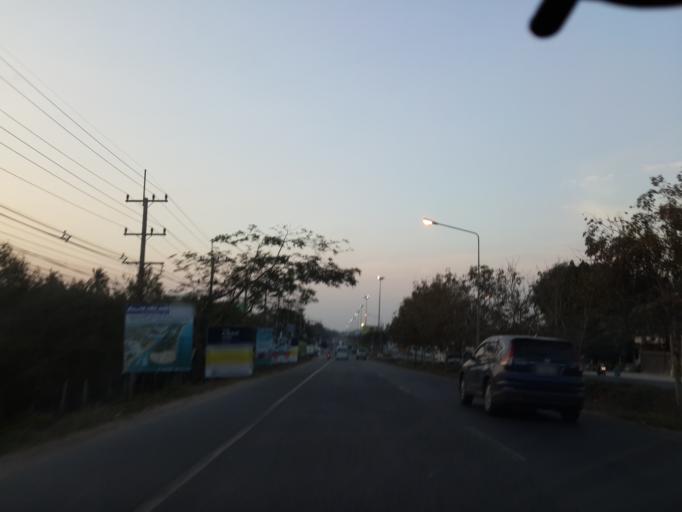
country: TH
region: Chon Buri
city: Phatthaya
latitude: 12.8644
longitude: 100.9057
